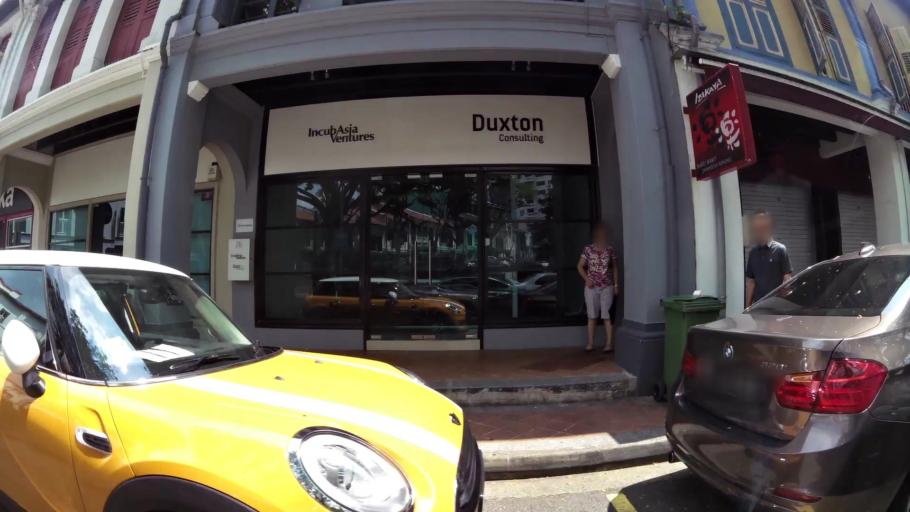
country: SG
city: Singapore
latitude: 1.2792
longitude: 103.8433
